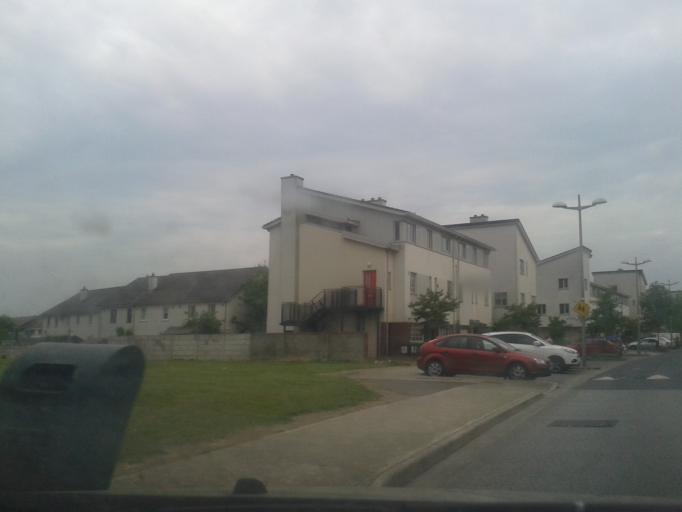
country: IE
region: Leinster
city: Ballymun
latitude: 53.3981
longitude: -6.2714
